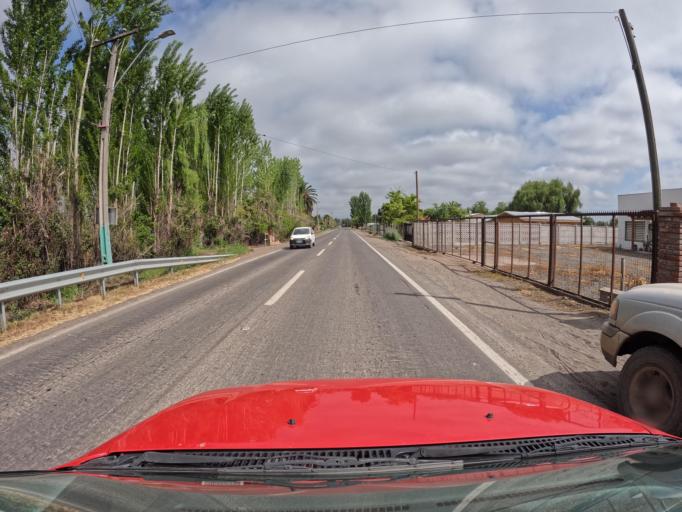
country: CL
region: O'Higgins
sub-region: Provincia de Colchagua
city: Santa Cruz
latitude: -34.6828
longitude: -71.3352
